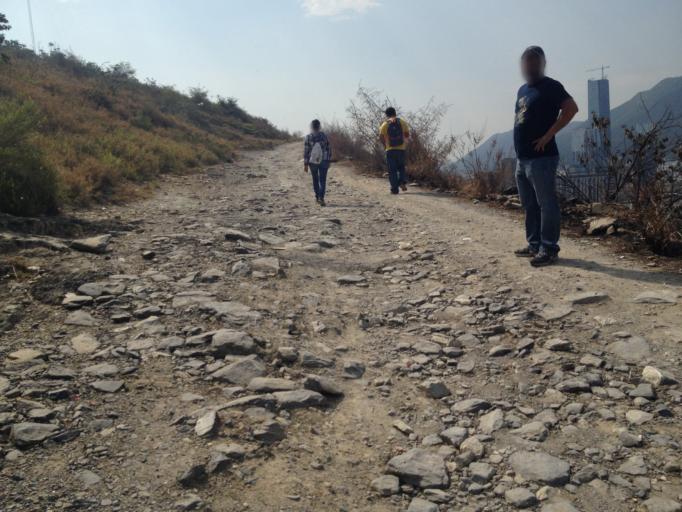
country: MX
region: Nuevo Leon
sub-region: Monterrey
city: Monterrey
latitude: 25.6538
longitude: -100.3296
